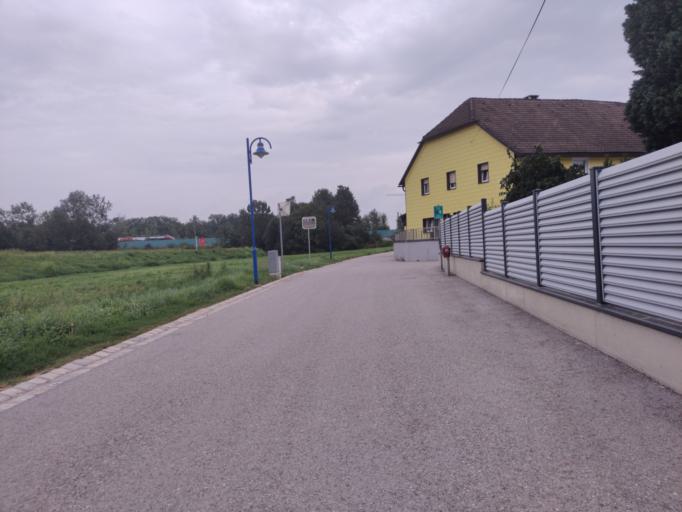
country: AT
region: Lower Austria
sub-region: Politischer Bezirk Amstetten
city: Ennsdorf
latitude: 48.2165
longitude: 14.4910
